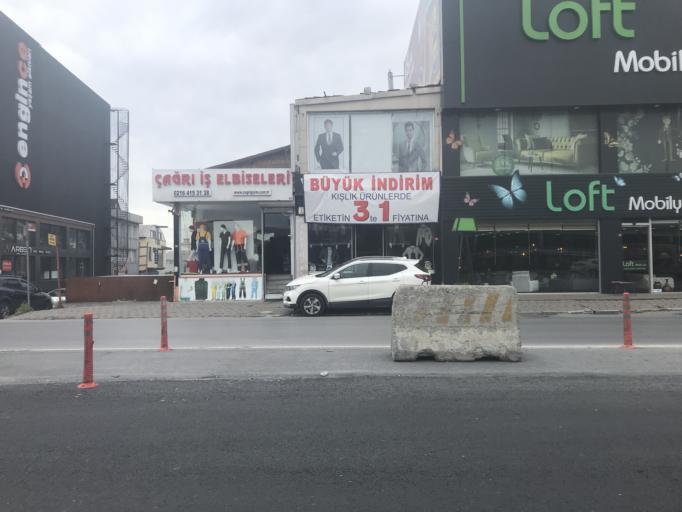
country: TR
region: Istanbul
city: Umraniye
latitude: 41.0012
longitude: 29.1566
